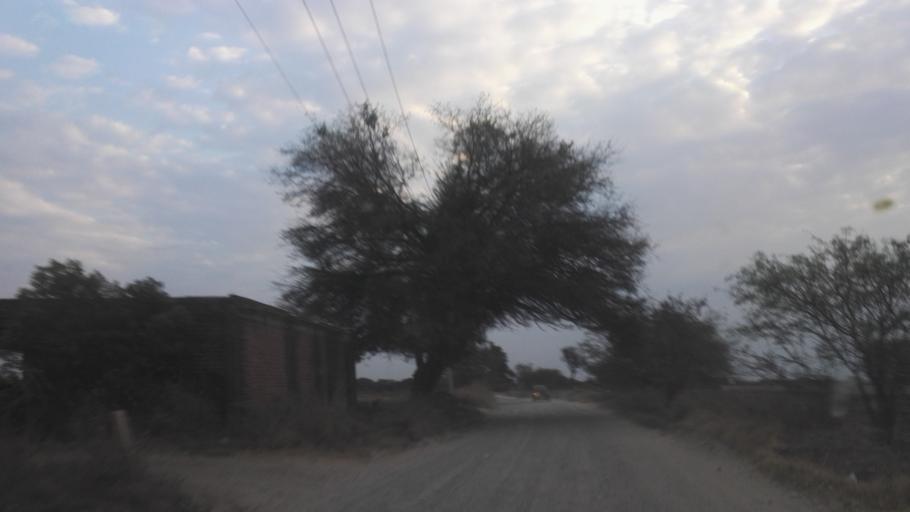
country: MX
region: Guanajuato
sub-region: Leon
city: Ladrilleras del Refugio
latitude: 21.0817
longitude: -101.5565
